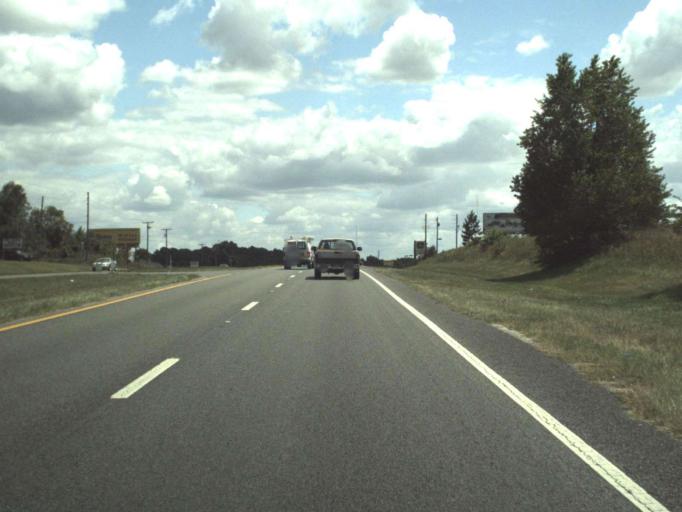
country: US
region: Florida
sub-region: Marion County
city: Ocala
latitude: 29.2561
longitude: -82.1522
